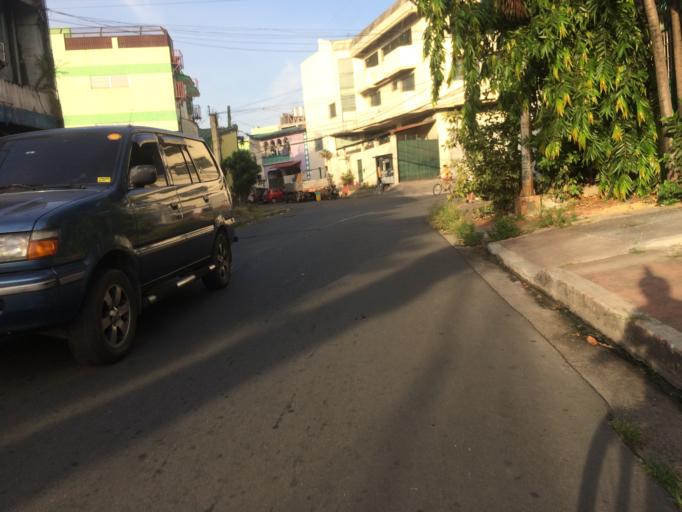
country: PH
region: Calabarzon
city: Bagong Pagasa
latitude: 14.6723
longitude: 121.0235
